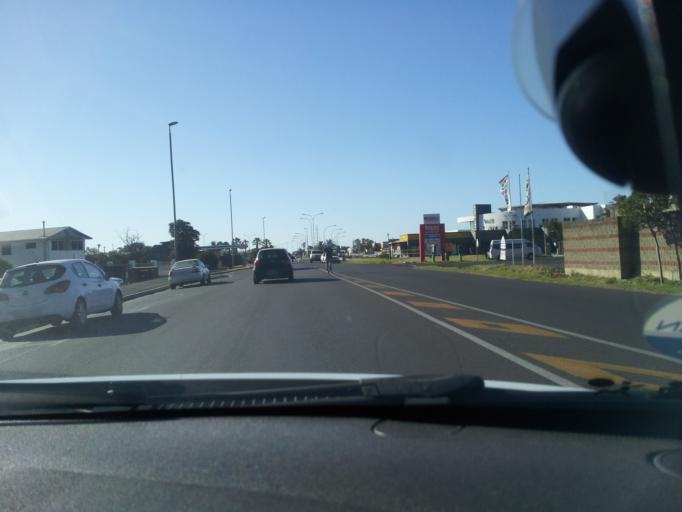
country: ZA
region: Western Cape
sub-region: Overberg District Municipality
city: Grabouw
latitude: -34.1549
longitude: 18.8686
